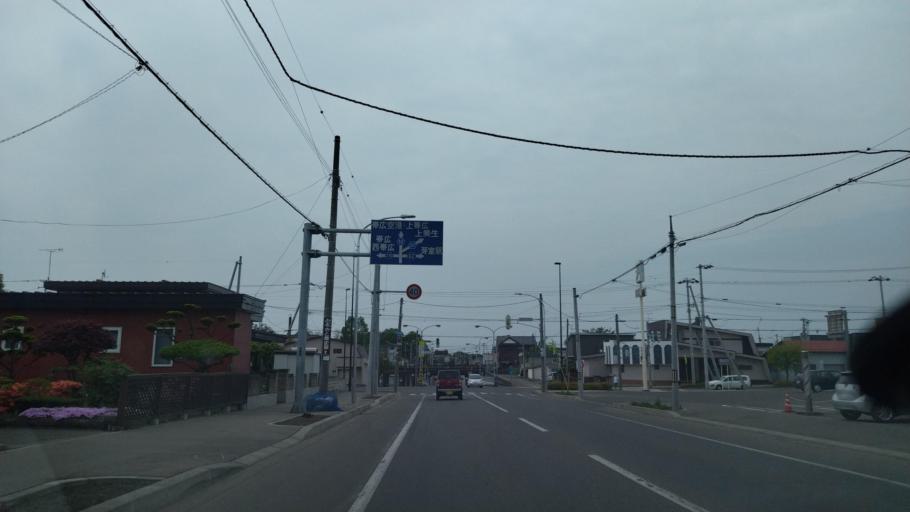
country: JP
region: Hokkaido
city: Obihiro
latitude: 42.9119
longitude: 143.0543
